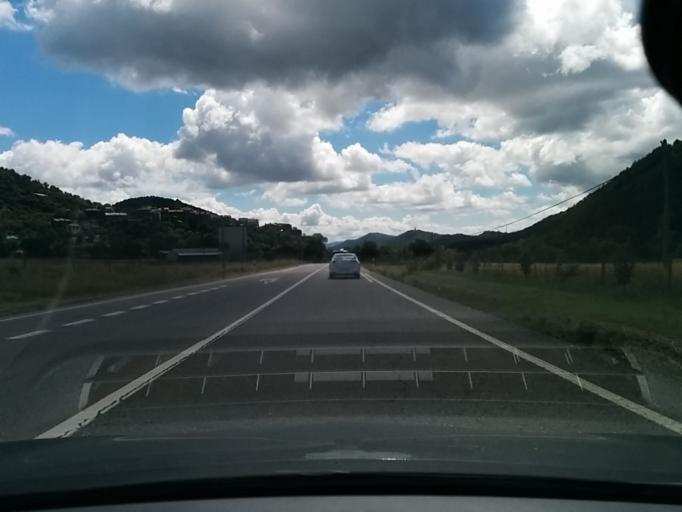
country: ES
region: Aragon
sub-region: Provincia de Huesca
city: Boltana
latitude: 42.4488
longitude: 0.0595
